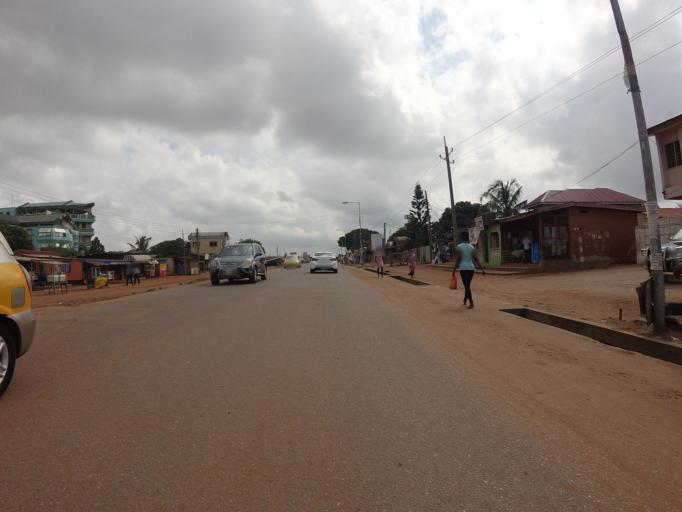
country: GH
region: Greater Accra
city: Teshi Old Town
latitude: 5.6074
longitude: -0.1127
